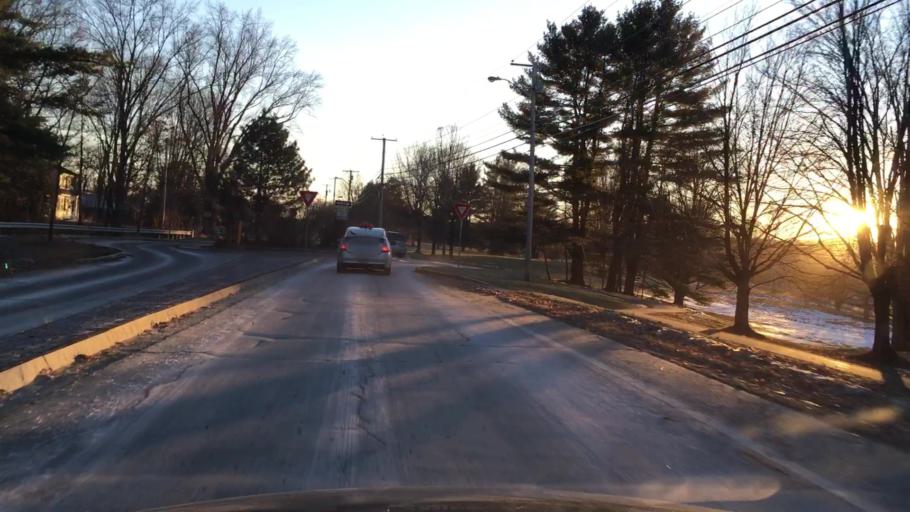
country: US
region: New Hampshire
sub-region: Grafton County
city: Hanover
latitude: 43.7281
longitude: -72.2685
